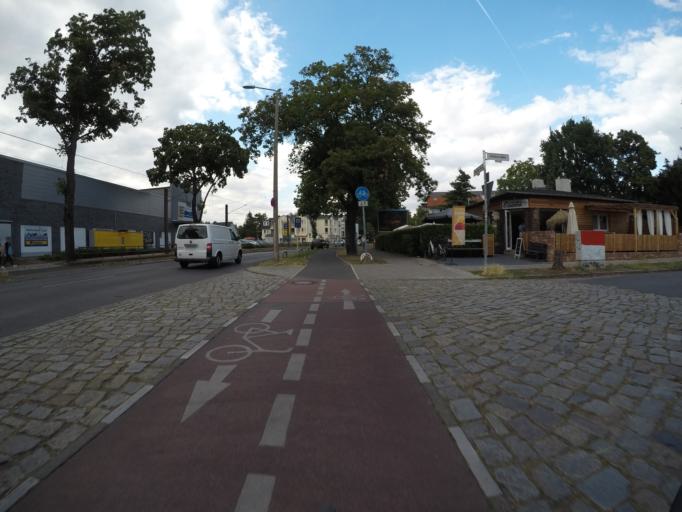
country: DE
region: Berlin
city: Mahlsdorf
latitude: 52.4818
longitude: 13.6014
